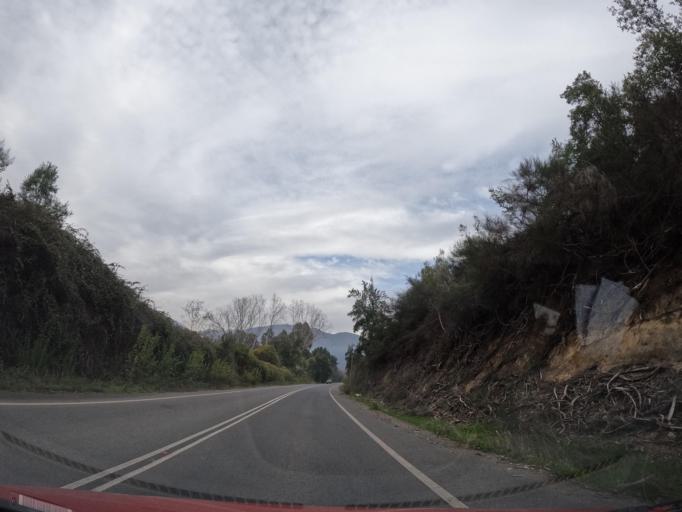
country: CL
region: Maule
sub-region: Provincia de Linares
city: Colbun
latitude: -35.6649
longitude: -71.2388
